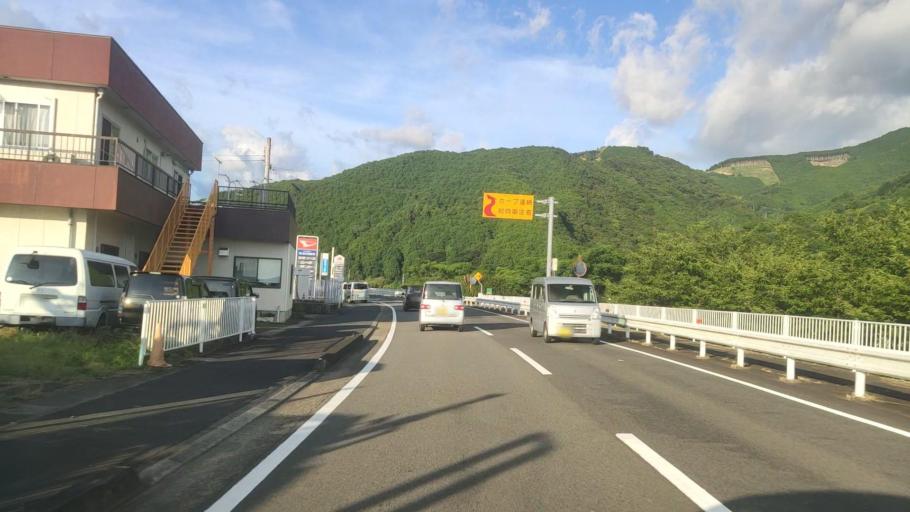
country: JP
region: Wakayama
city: Tanabe
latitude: 33.7187
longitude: 135.4800
